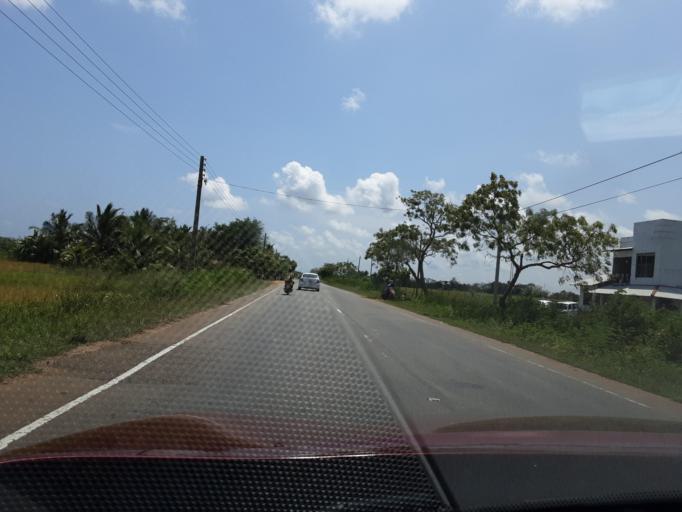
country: LK
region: Southern
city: Tangalla
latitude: 6.2179
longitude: 81.2128
